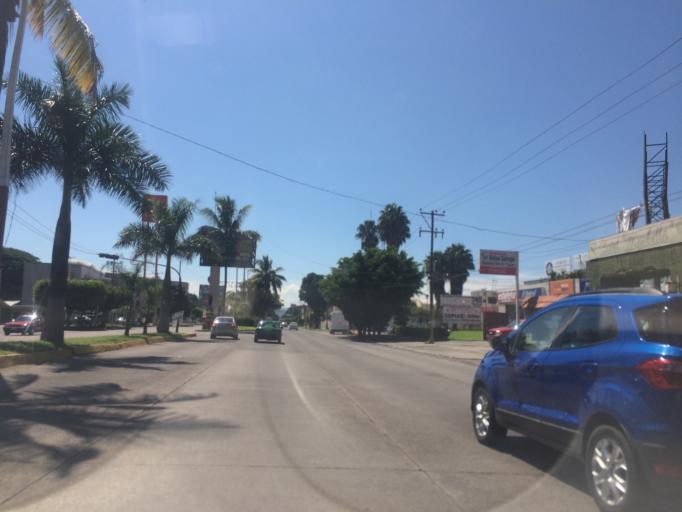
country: MX
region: Nayarit
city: Tepic
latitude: 21.4974
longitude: -104.8853
